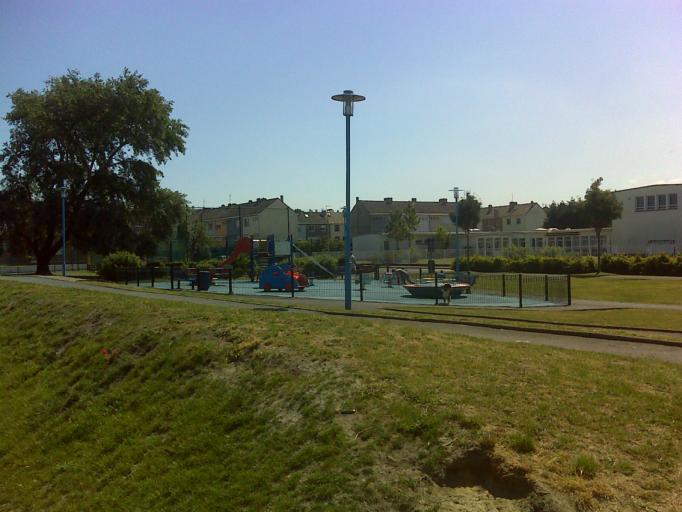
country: FR
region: Nord-Pas-de-Calais
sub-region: Departement du Nord
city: Teteghem
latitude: 51.0492
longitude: 2.4274
